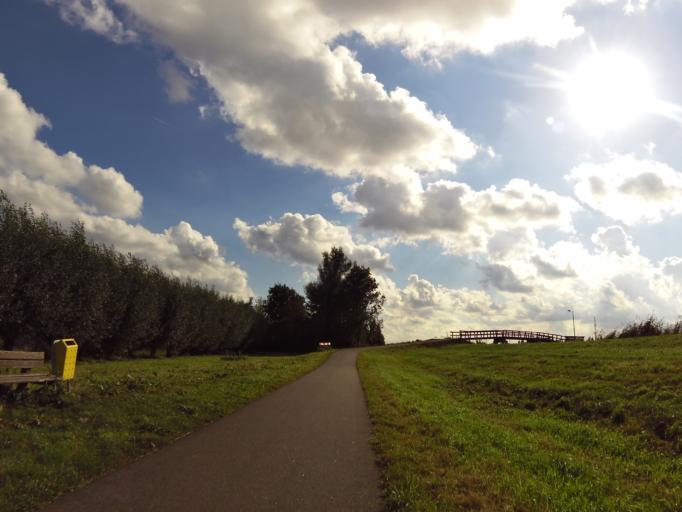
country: NL
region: South Holland
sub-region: Gemeente Alphen aan den Rijn
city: Alphen aan den Rijn
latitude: 52.1055
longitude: 4.6007
